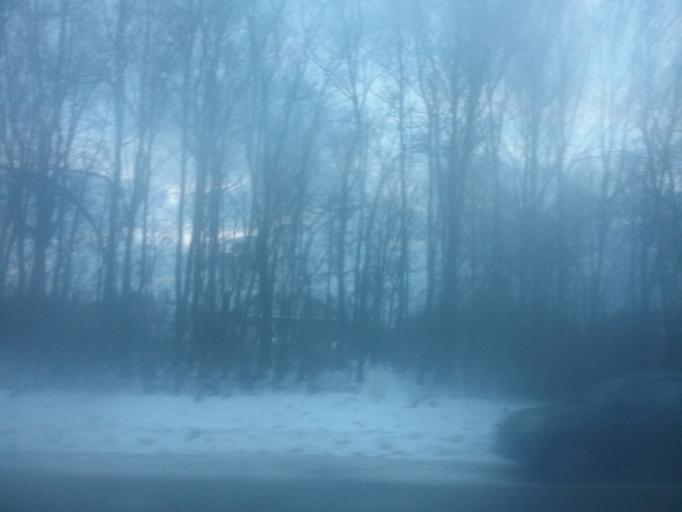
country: RU
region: Tula
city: Kireyevsk
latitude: 54.0200
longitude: 37.9160
